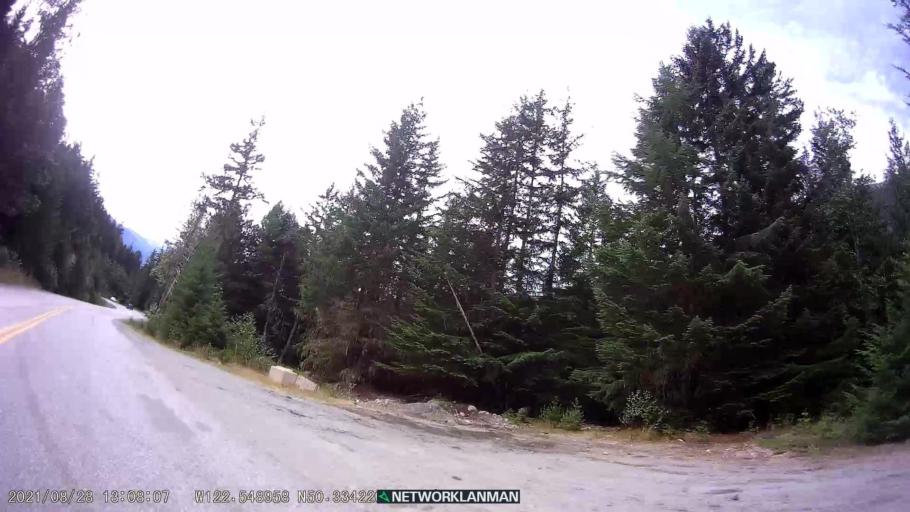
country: CA
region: British Columbia
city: Pemberton
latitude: 50.3343
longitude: -122.5492
